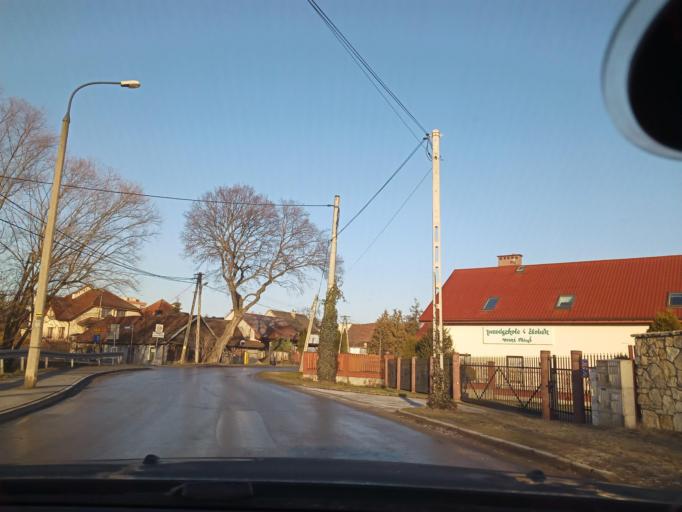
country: PL
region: Lesser Poland Voivodeship
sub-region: Powiat krakowski
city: Michalowice
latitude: 50.0954
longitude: 20.0271
